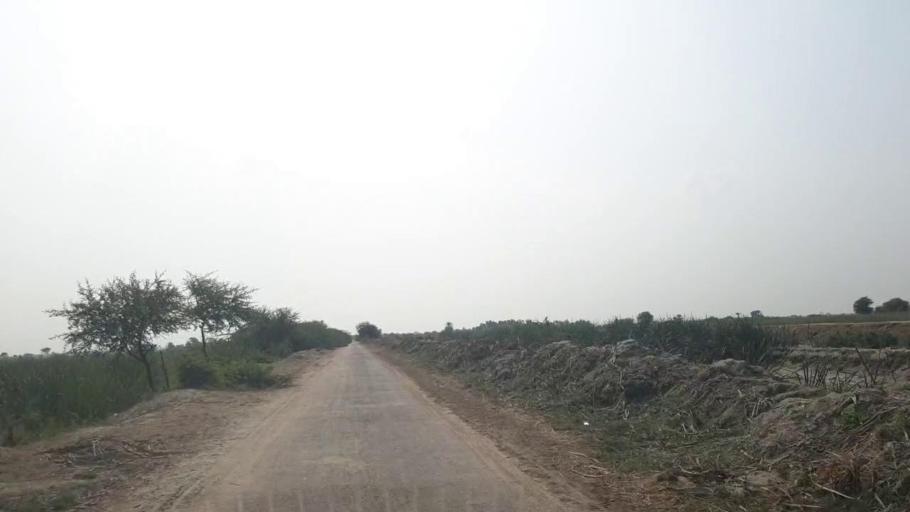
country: PK
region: Sindh
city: Badin
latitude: 24.7229
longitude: 68.7347
